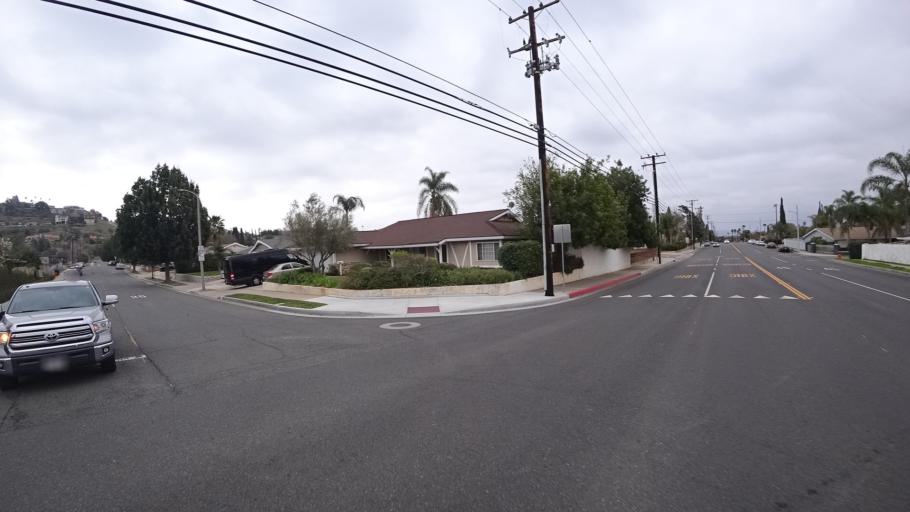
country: US
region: California
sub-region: Orange County
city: North Tustin
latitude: 33.7789
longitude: -117.8097
